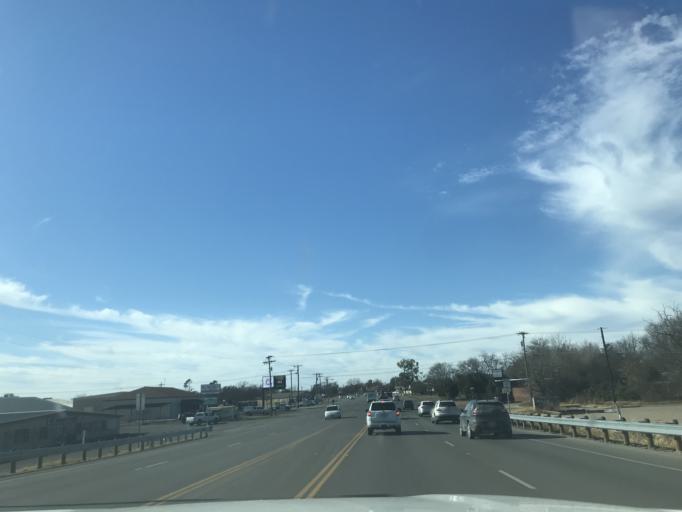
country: US
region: Texas
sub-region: Erath County
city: Stephenville
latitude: 32.2065
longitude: -98.2212
